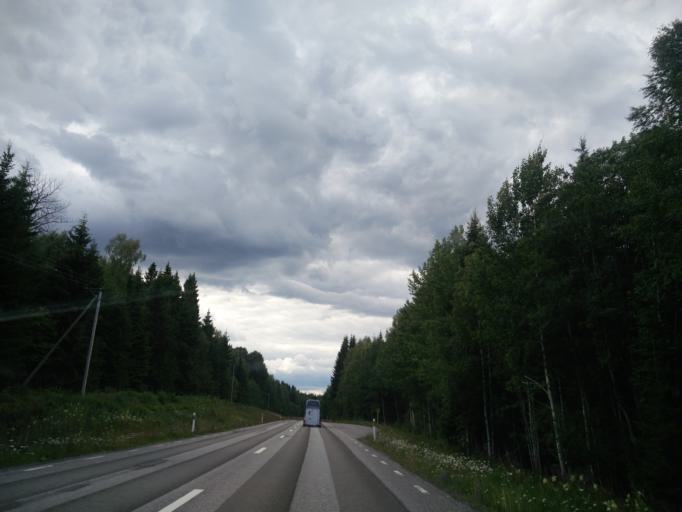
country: SE
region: OErebro
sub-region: Hallefors Kommun
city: Haellefors
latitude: 59.7721
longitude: 14.3969
